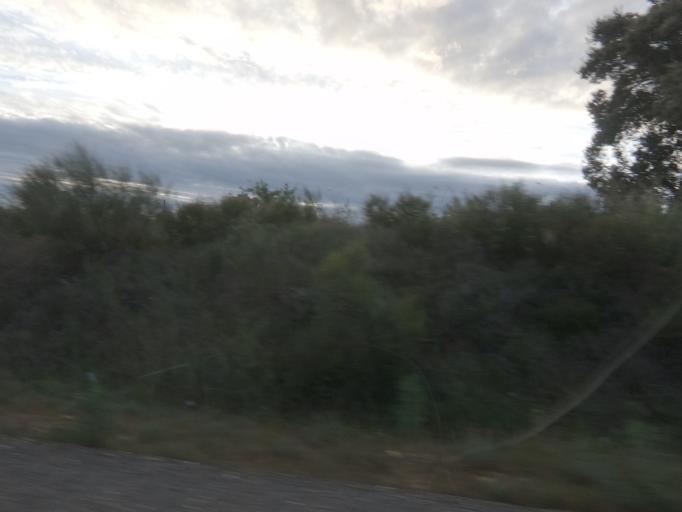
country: ES
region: Extremadura
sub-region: Provincia de Badajoz
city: La Roca de la Sierra
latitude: 39.1266
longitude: -6.6664
